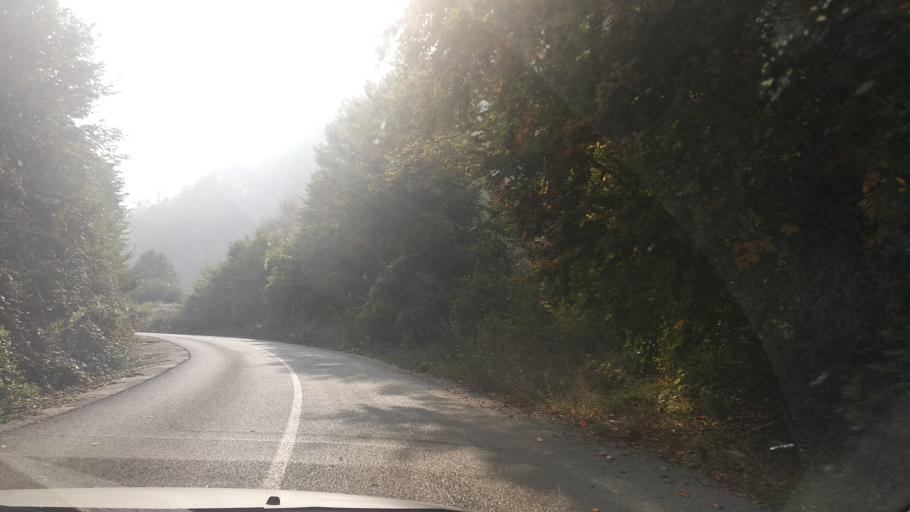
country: TR
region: Duzce
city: Kaynasli
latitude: 40.7086
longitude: 31.2652
